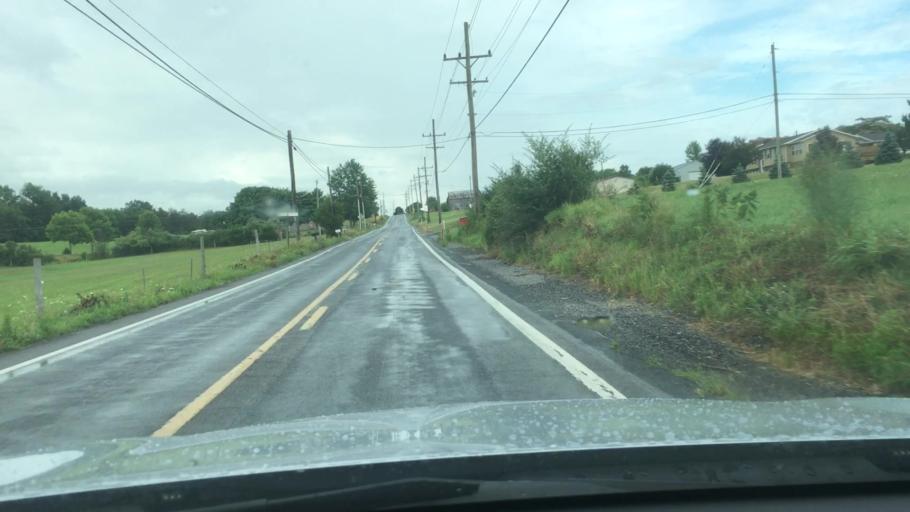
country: US
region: Pennsylvania
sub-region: Franklin County
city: Greencastle
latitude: 39.8656
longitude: -77.7730
